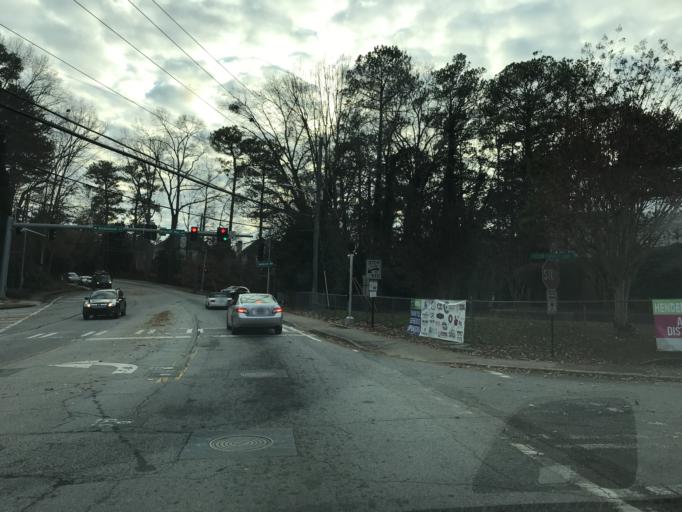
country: US
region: Georgia
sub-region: DeKalb County
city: Tucker
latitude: 33.8555
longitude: -84.2588
